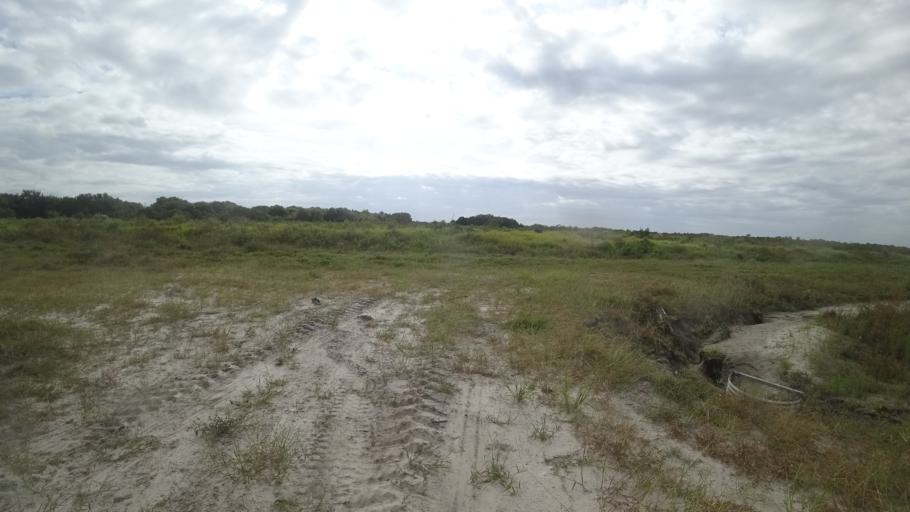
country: US
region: Florida
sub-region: Hillsborough County
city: Wimauma
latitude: 27.5818
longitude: -82.3079
